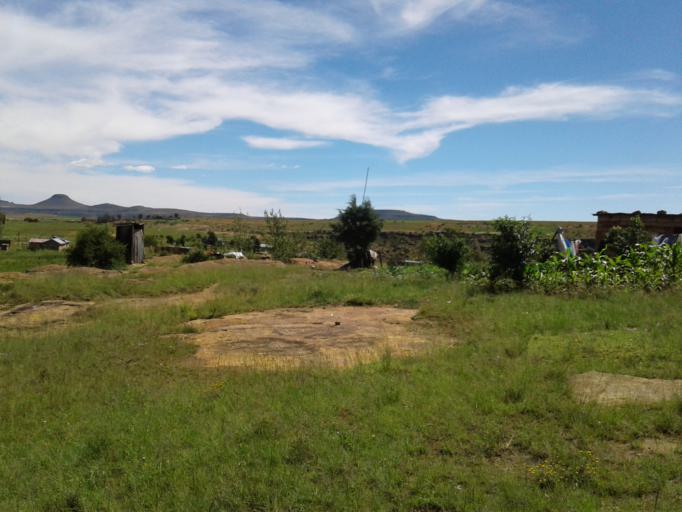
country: LS
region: Quthing
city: Quthing
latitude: -30.3369
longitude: 27.5325
